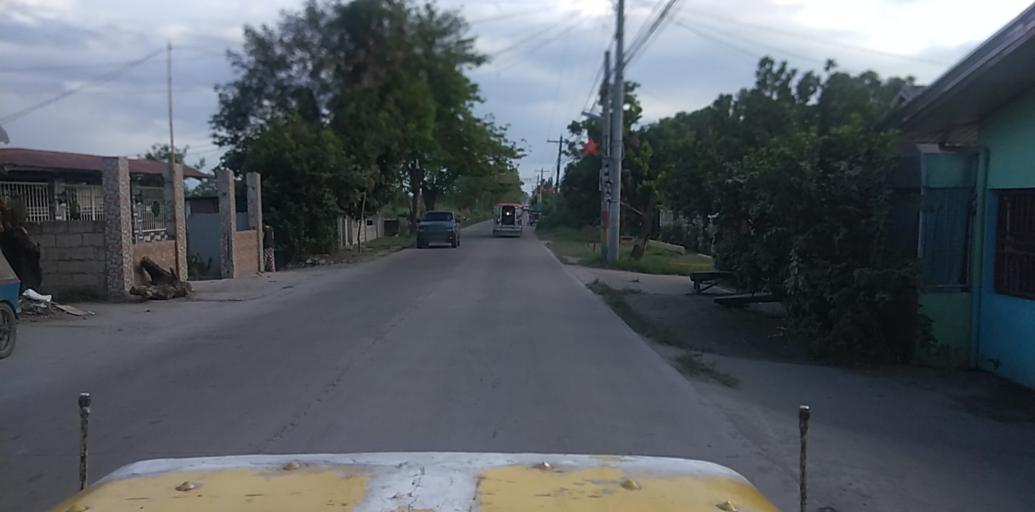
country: PH
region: Central Luzon
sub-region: Province of Pampanga
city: San Antonio
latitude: 15.1511
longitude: 120.6892
